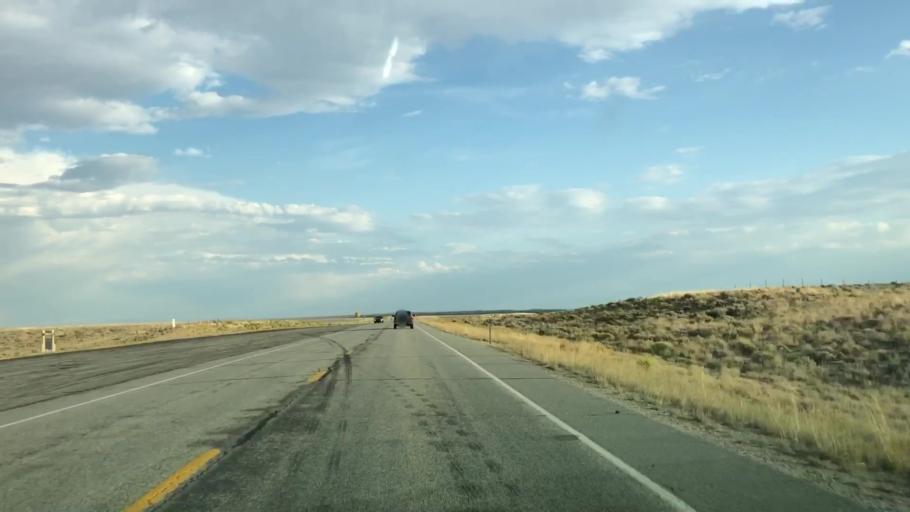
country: US
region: Wyoming
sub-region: Sublette County
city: Marbleton
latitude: 42.3281
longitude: -109.5140
